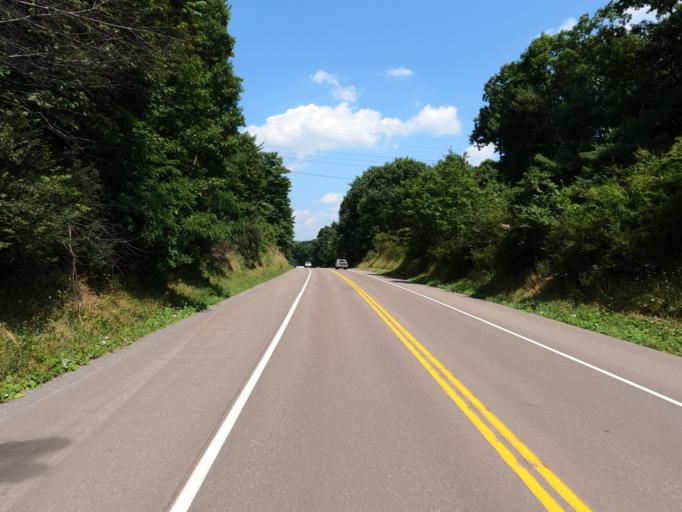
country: US
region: Maryland
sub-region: Garrett County
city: Mountain Lake Park
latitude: 39.4457
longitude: -79.3762
